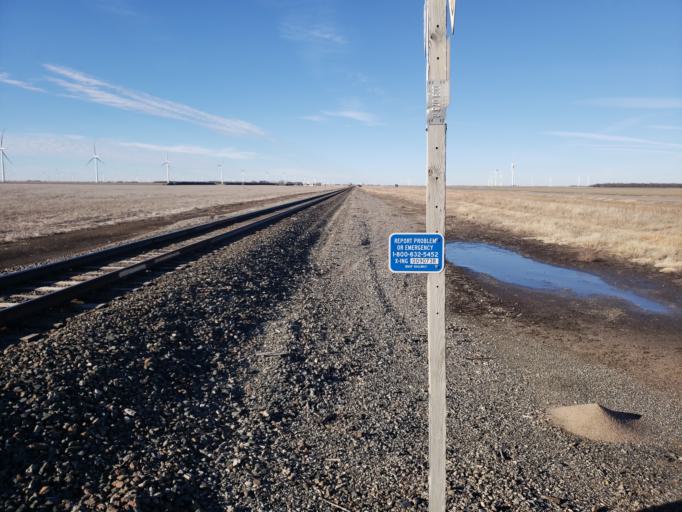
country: US
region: Kansas
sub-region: Edwards County
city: Kinsley
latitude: 37.8885
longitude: -99.5701
